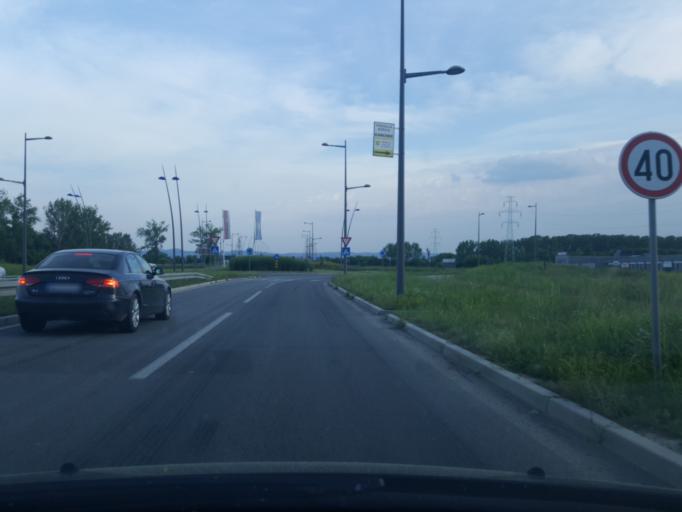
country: RS
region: Autonomna Pokrajina Vojvodina
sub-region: Juznobacki Okrug
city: Novi Sad
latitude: 45.2888
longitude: 19.8064
